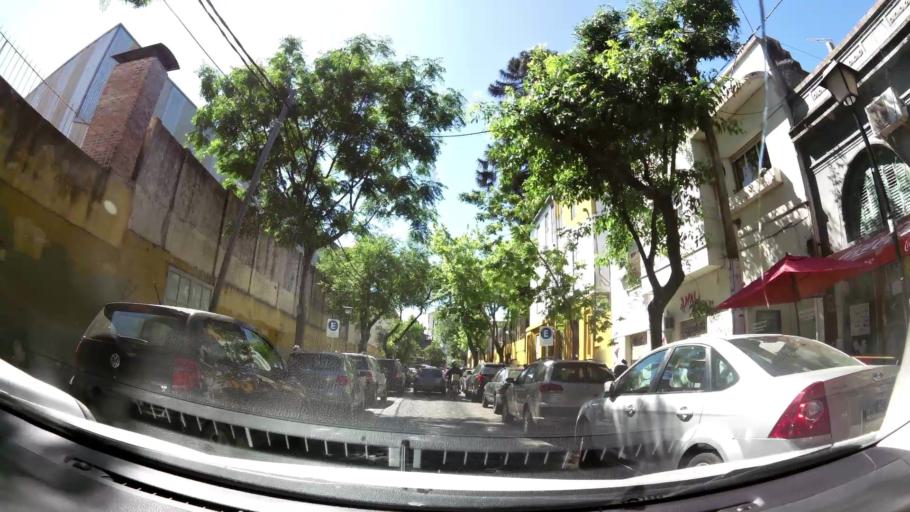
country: AR
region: Buenos Aires
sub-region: Partido de San Isidro
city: San Isidro
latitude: -34.4715
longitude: -58.5101
